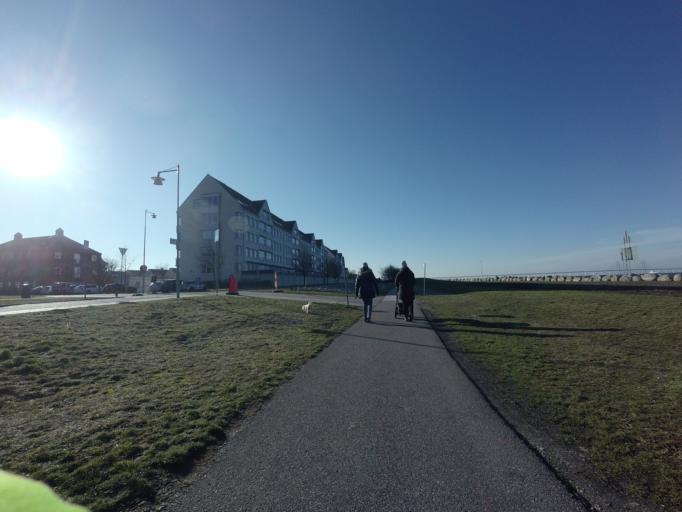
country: SE
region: Skane
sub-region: Malmo
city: Bunkeflostrand
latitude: 55.5909
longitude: 12.9197
